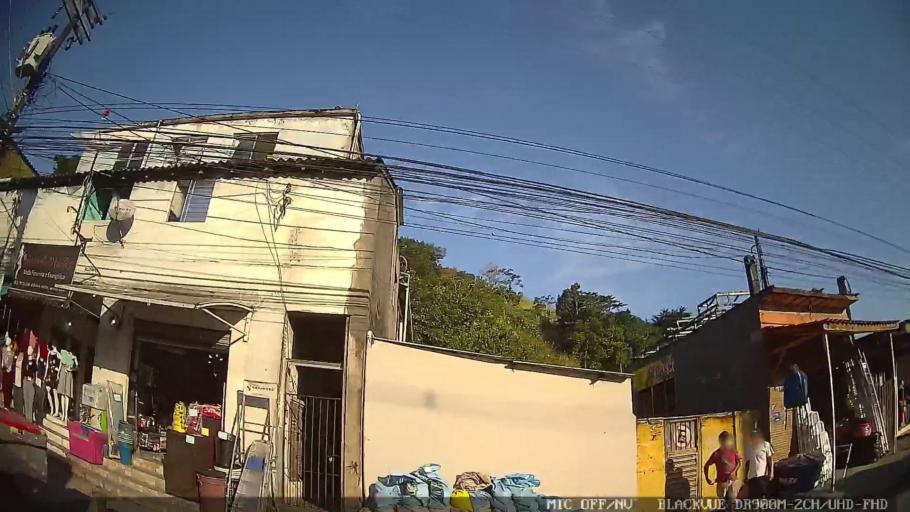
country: BR
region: Sao Paulo
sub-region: Guaruja
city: Guaruja
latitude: -23.9768
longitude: -46.2590
